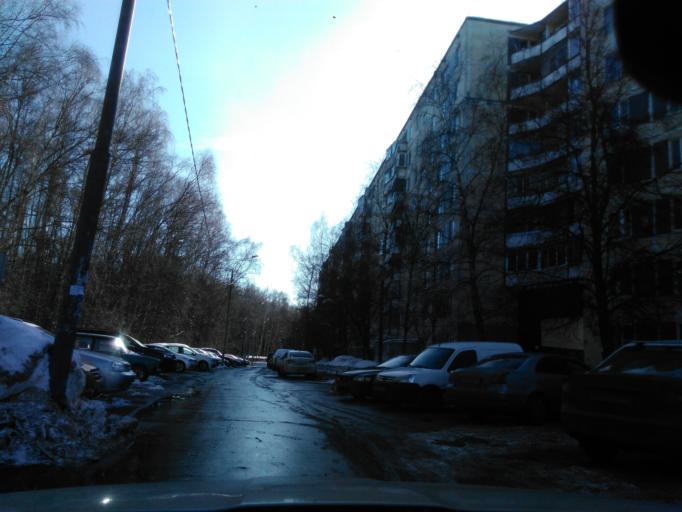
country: RU
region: Moscow
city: Zelenograd
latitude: 55.9792
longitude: 37.1941
